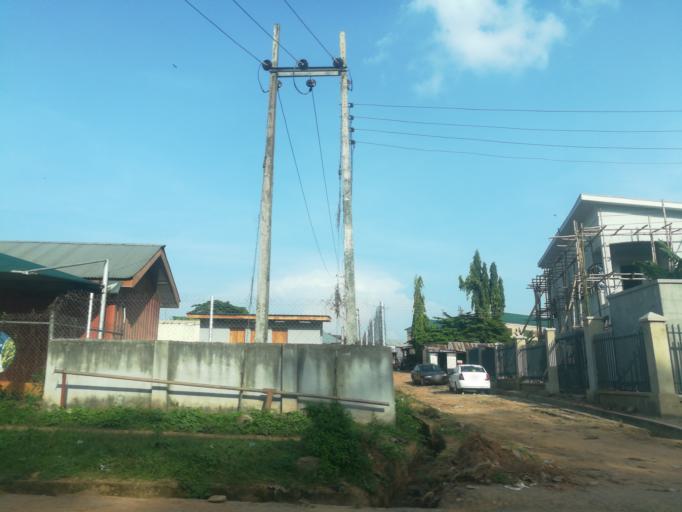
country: NG
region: Oyo
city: Moniya
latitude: 7.4993
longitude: 3.9134
